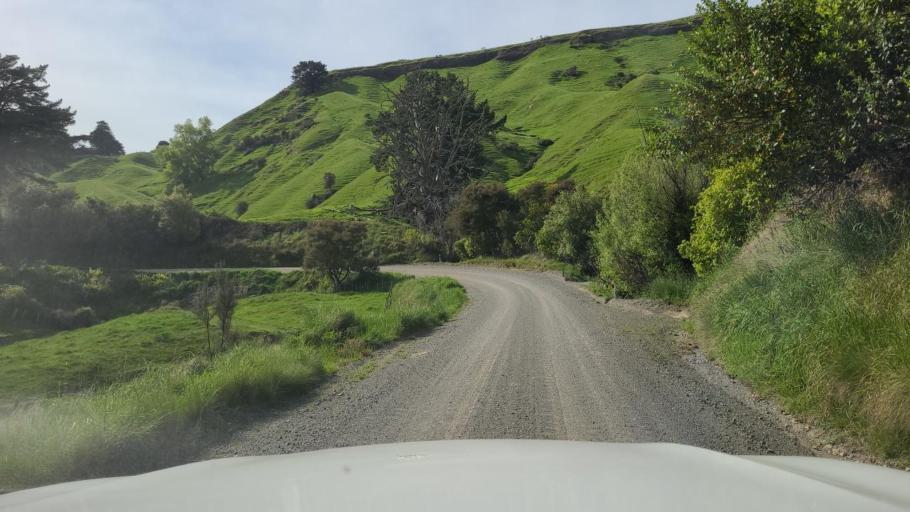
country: NZ
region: Hawke's Bay
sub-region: Napier City
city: Taradale
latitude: -39.3393
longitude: 176.6581
